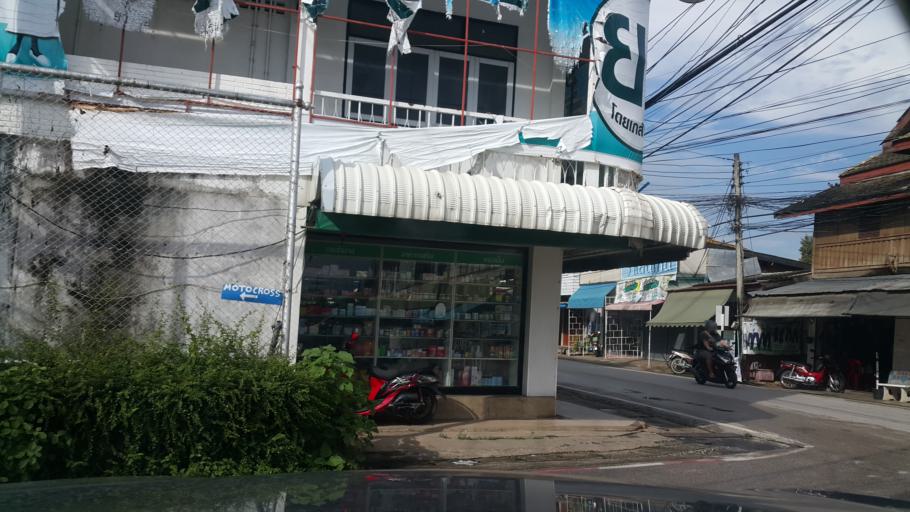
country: TH
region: Lampang
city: Thoen
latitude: 17.6030
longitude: 99.2085
